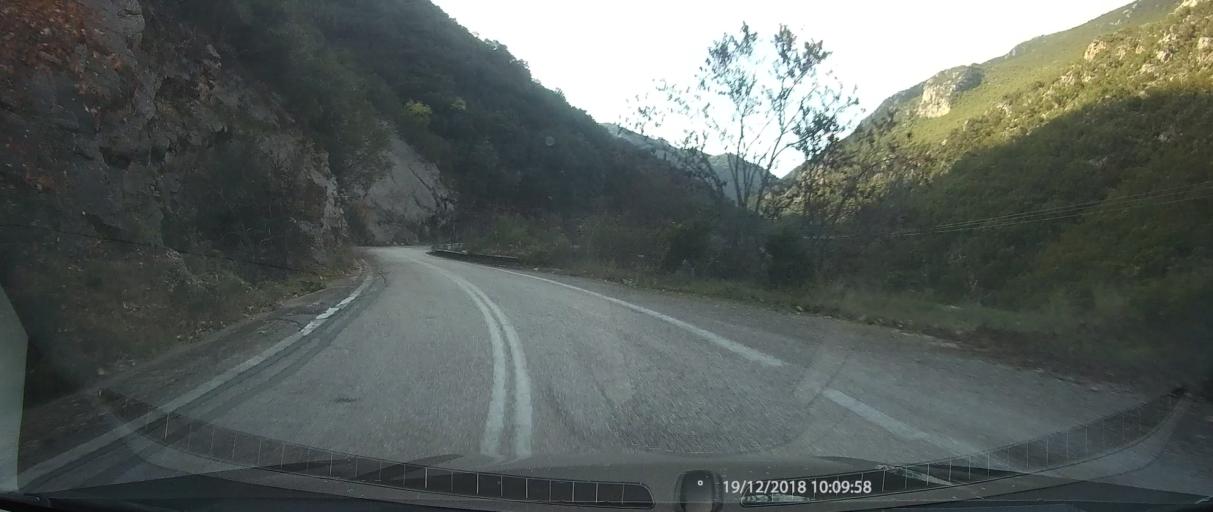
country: GR
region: Peloponnese
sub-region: Nomos Messinias
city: Kalamata
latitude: 37.1069
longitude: 22.1863
